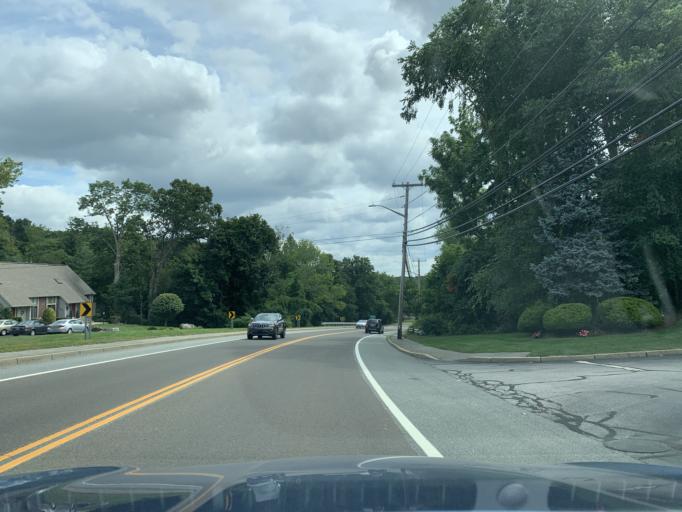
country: US
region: Rhode Island
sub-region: Providence County
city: Johnston
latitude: 41.7788
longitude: -71.4859
